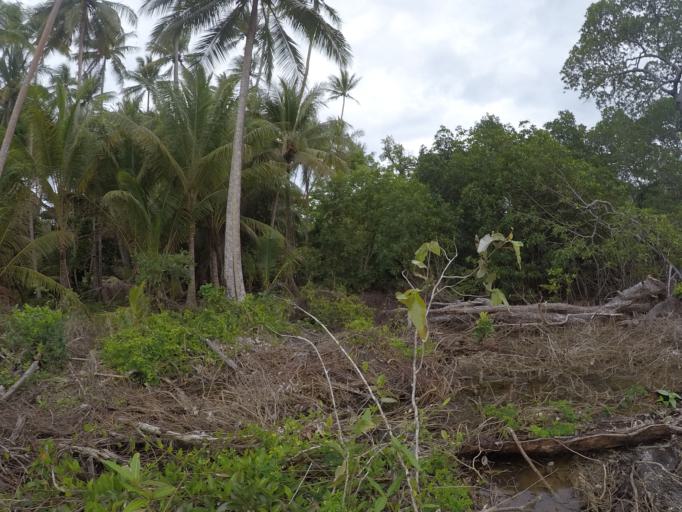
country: PG
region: Milne Bay
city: Alotau
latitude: -10.2623
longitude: 150.8115
